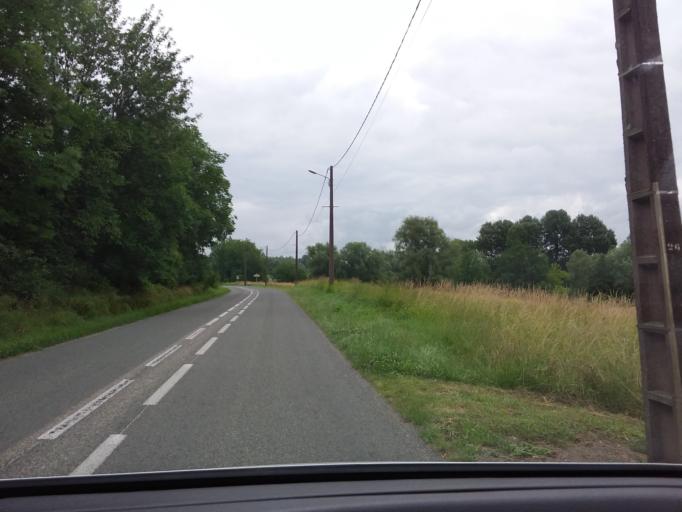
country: FR
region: Picardie
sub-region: Departement de l'Aisne
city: Vailly-sur-Aisne
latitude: 49.4025
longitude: 3.5657
